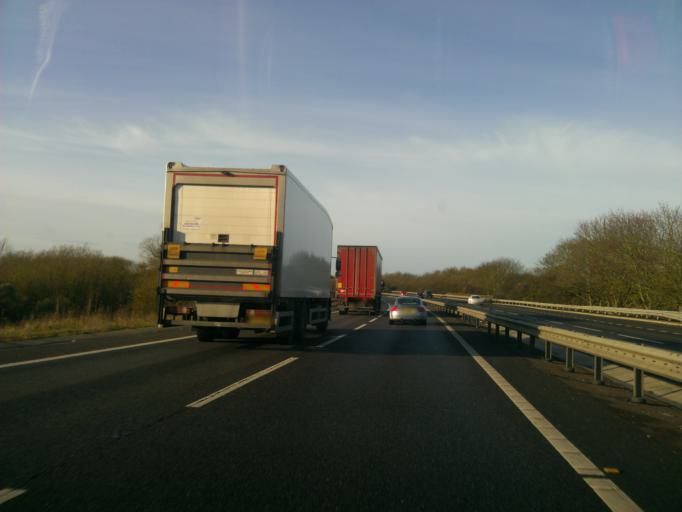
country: GB
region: England
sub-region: Essex
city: Kelvedon
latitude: 51.8270
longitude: 0.6943
